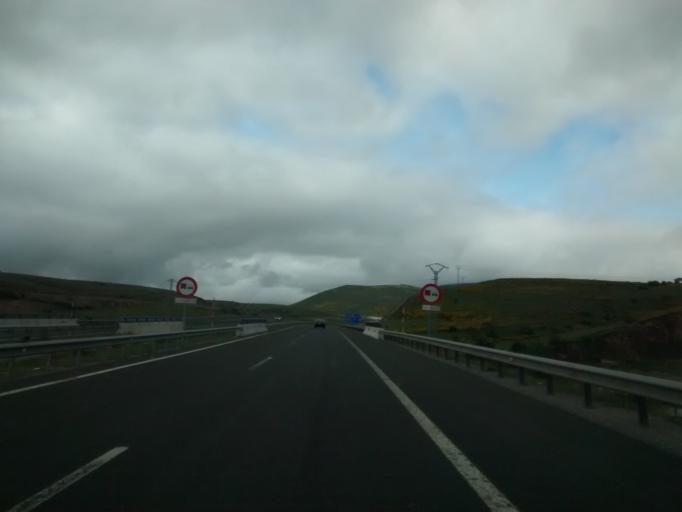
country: ES
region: Cantabria
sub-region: Provincia de Cantabria
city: Mataporquera
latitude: 42.8939
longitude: -4.1259
